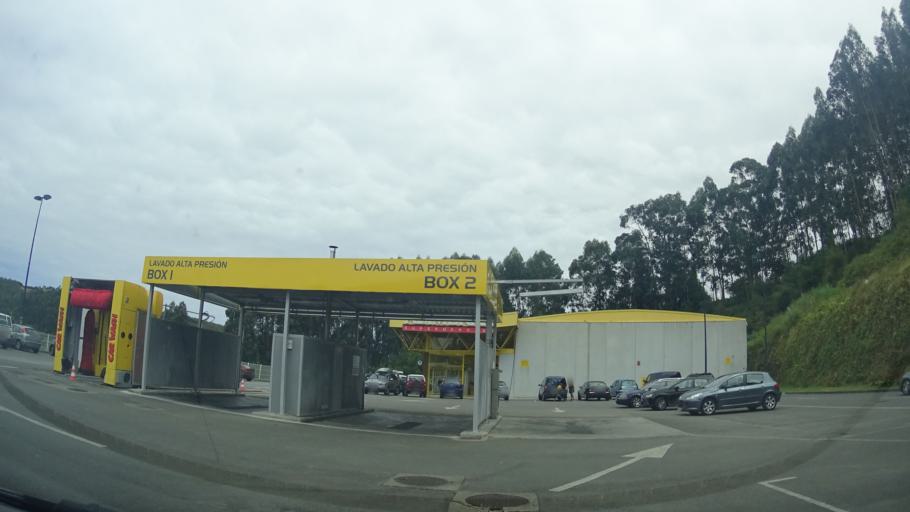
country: ES
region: Asturias
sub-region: Province of Asturias
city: Ribadesella
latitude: 43.4644
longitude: -5.0892
